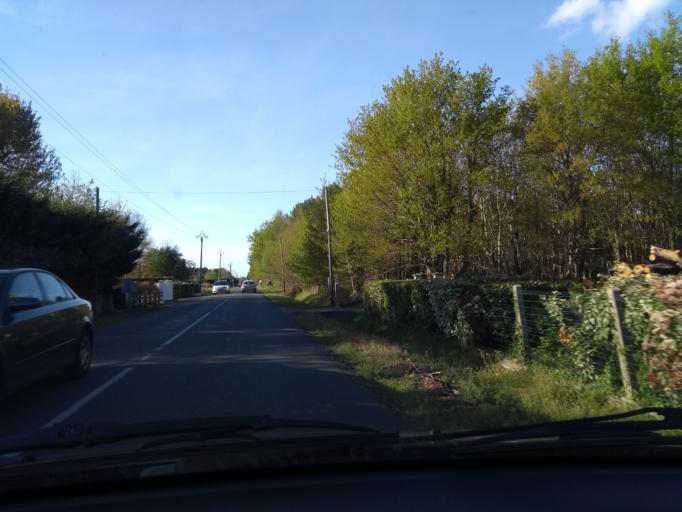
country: FR
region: Aquitaine
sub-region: Departement des Landes
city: Sanguinet
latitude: 44.4707
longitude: -1.0695
